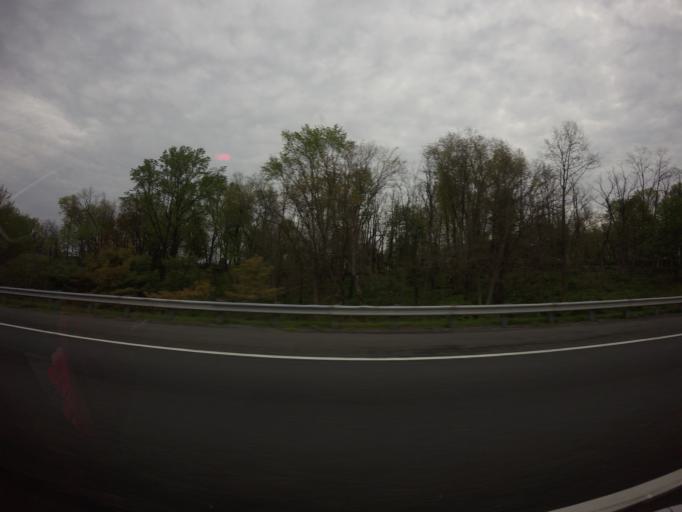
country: US
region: Maryland
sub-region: Frederick County
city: Linganore
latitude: 39.3753
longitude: -77.2301
